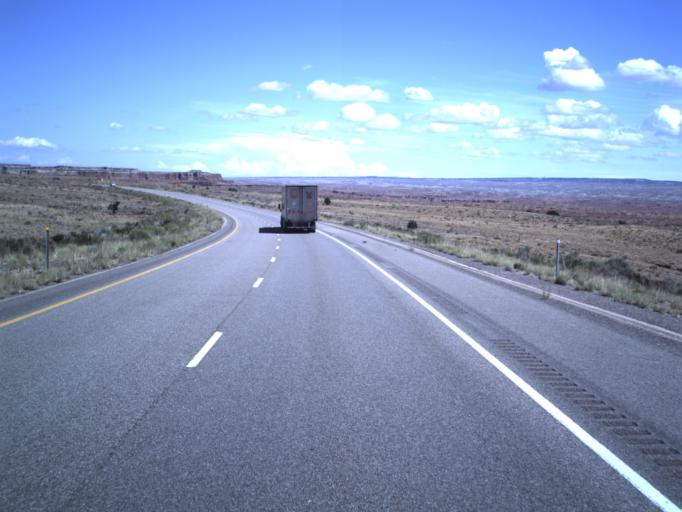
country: US
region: Utah
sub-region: Emery County
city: Ferron
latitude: 38.8311
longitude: -111.1087
